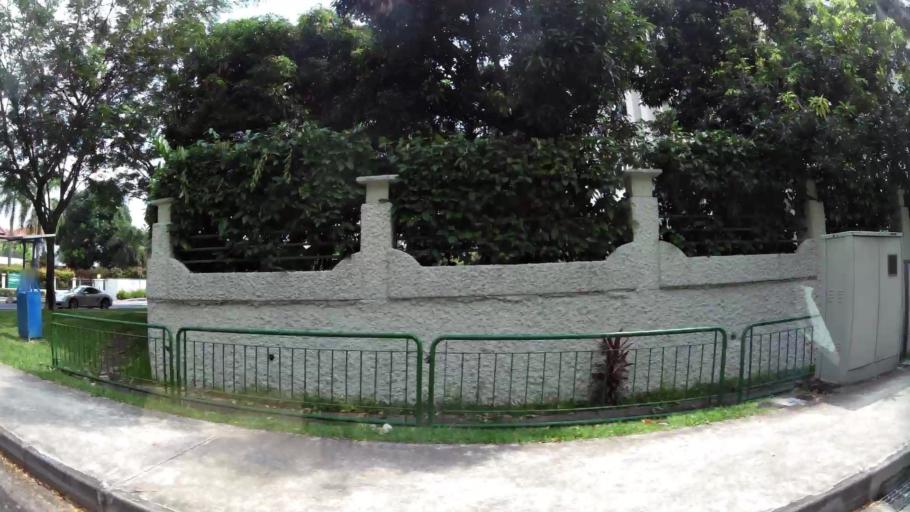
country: SG
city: Singapore
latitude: 1.3005
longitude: 103.8877
